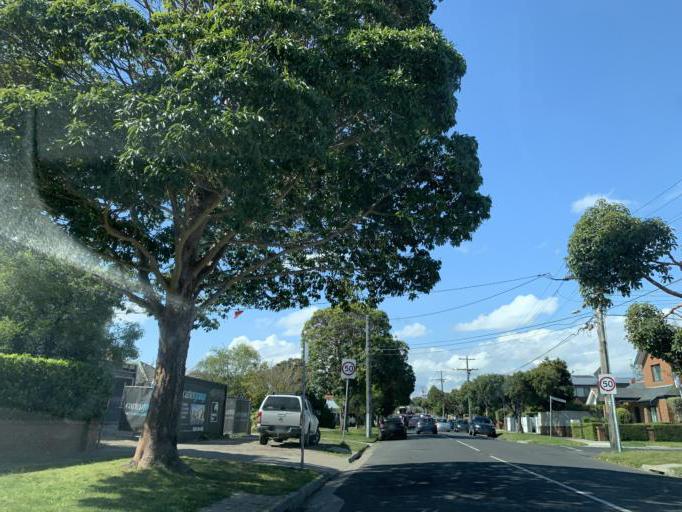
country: AU
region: Victoria
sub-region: Kingston
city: Parkdale
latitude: -37.9924
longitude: 145.0788
